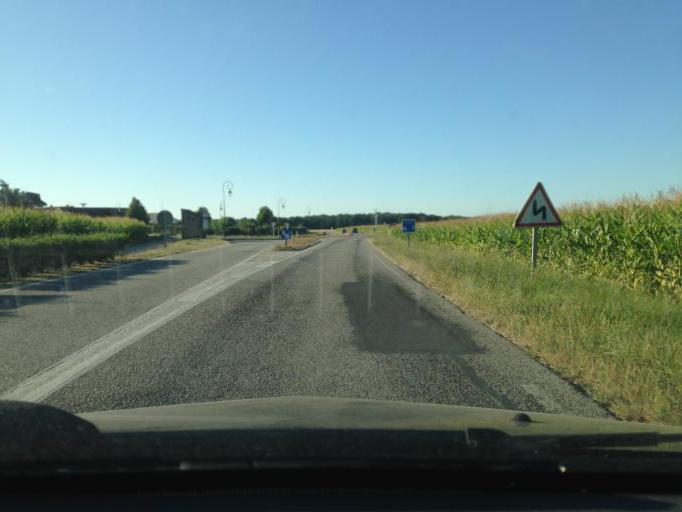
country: FR
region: Ile-de-France
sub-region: Departement des Yvelines
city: Magny-les-Hameaux
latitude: 48.7323
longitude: 2.0728
